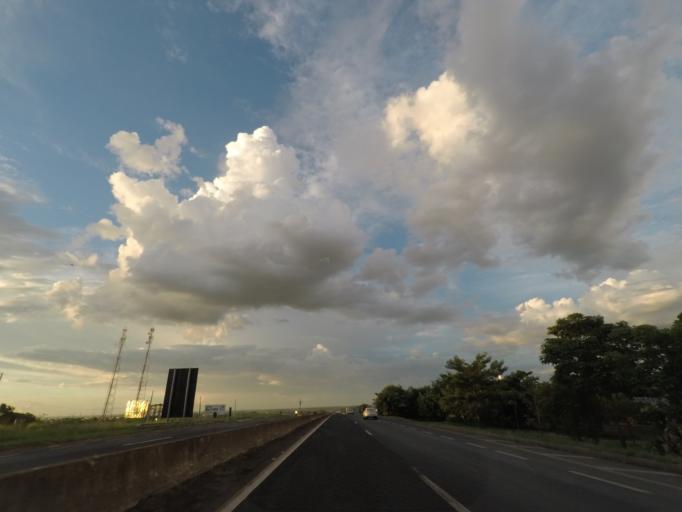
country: BR
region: Minas Gerais
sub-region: Uberaba
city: Uberaba
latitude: -19.7732
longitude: -47.9728
